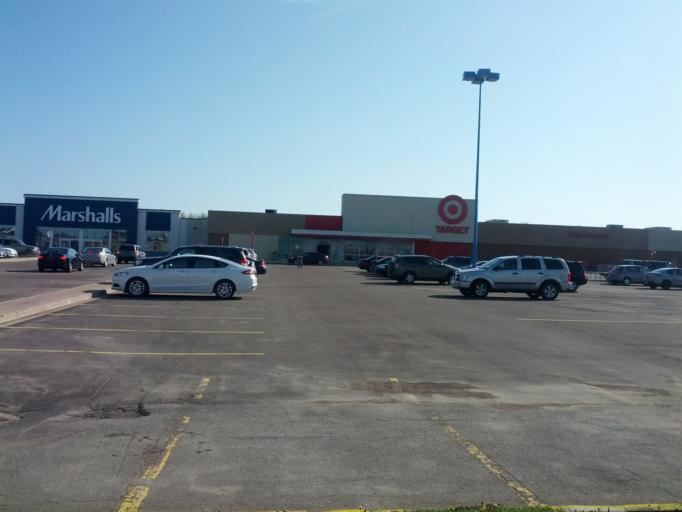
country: CA
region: New Brunswick
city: Moncton
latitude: 46.1109
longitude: -64.8325
